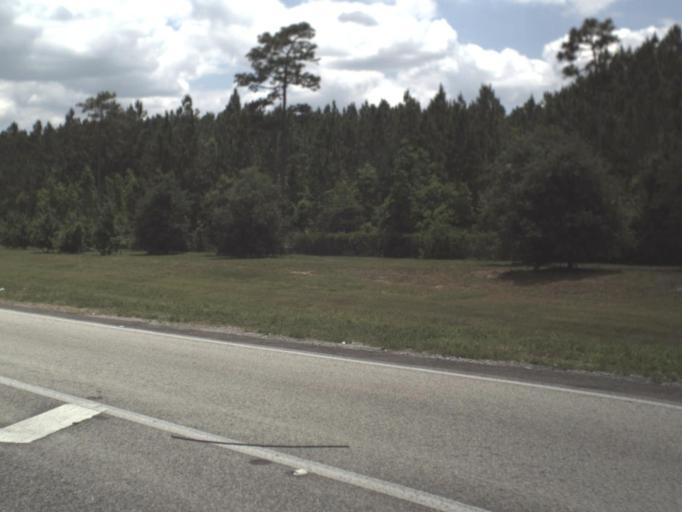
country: US
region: Florida
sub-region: Duval County
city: Jacksonville Beach
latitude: 30.2648
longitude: -81.5196
